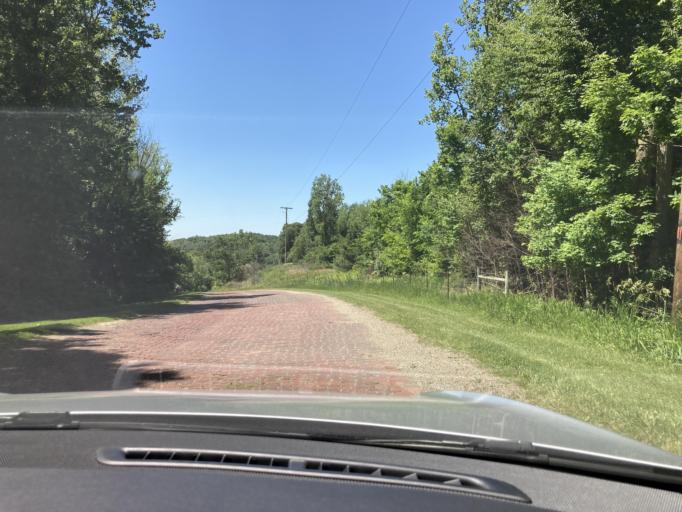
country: US
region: Ohio
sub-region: Carroll County
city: Malvern
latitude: 40.7581
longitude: -81.1849
